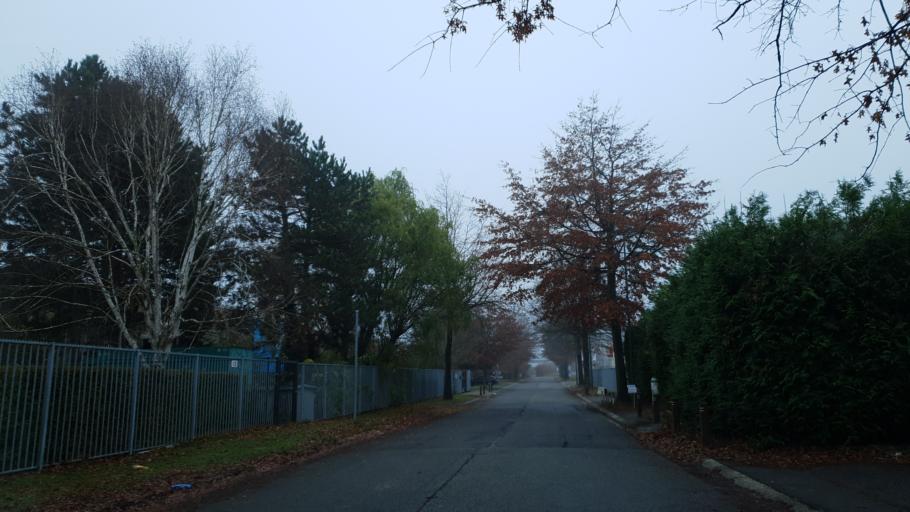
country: BE
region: Flanders
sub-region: Provincie Vlaams-Brabant
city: Zaventem
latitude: 50.8750
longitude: 4.4999
